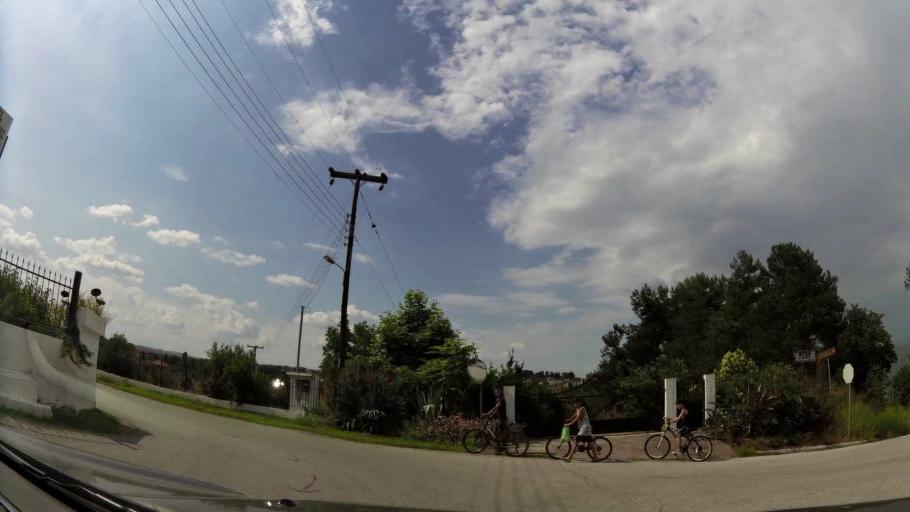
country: GR
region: Central Macedonia
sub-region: Nomos Pierias
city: Makrygialos
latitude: 40.4076
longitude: 22.6102
